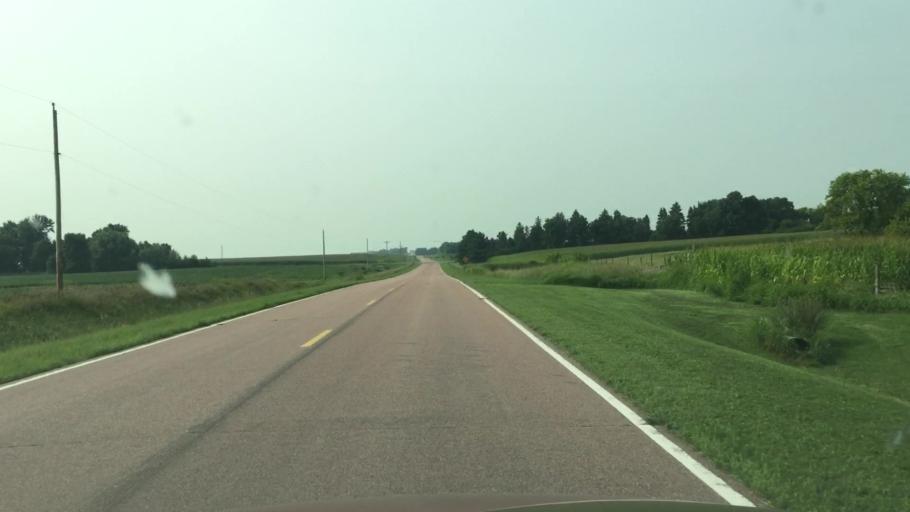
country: US
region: Iowa
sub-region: O'Brien County
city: Sheldon
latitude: 43.2480
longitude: -95.7833
